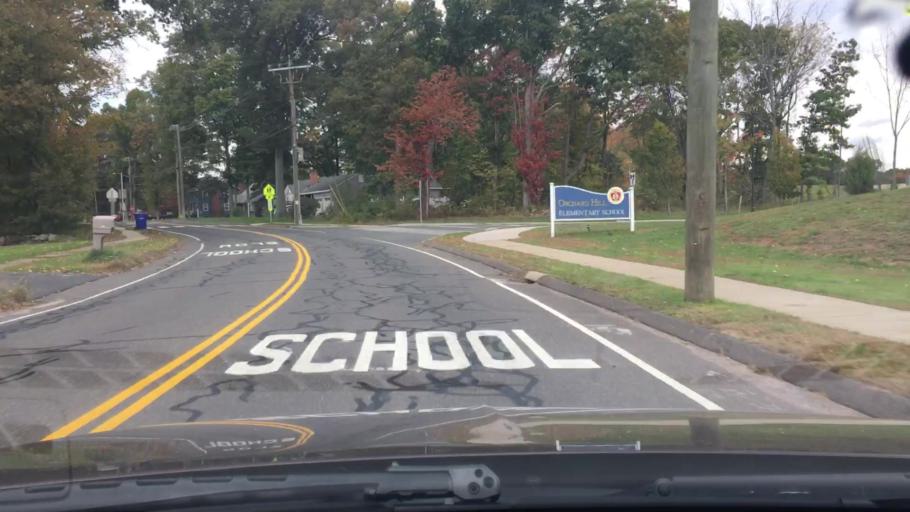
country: US
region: Connecticut
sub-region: Hartford County
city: Manchester
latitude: 41.8286
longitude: -72.5292
